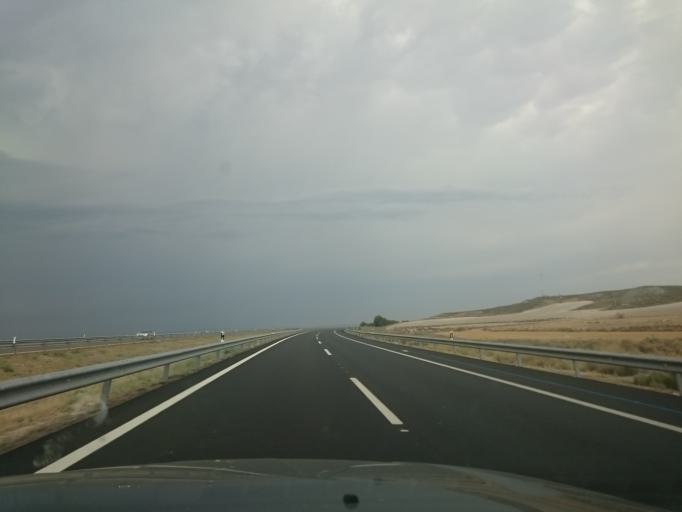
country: ES
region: Aragon
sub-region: Provincia de Zaragoza
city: Pina de Ebro
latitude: 41.5230
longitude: -0.4856
